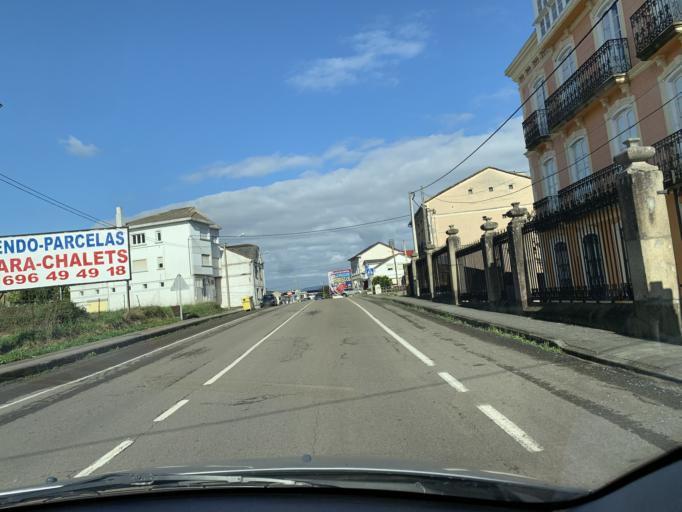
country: ES
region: Galicia
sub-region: Provincia de Lugo
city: Barreiros
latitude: 43.5398
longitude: -7.2393
